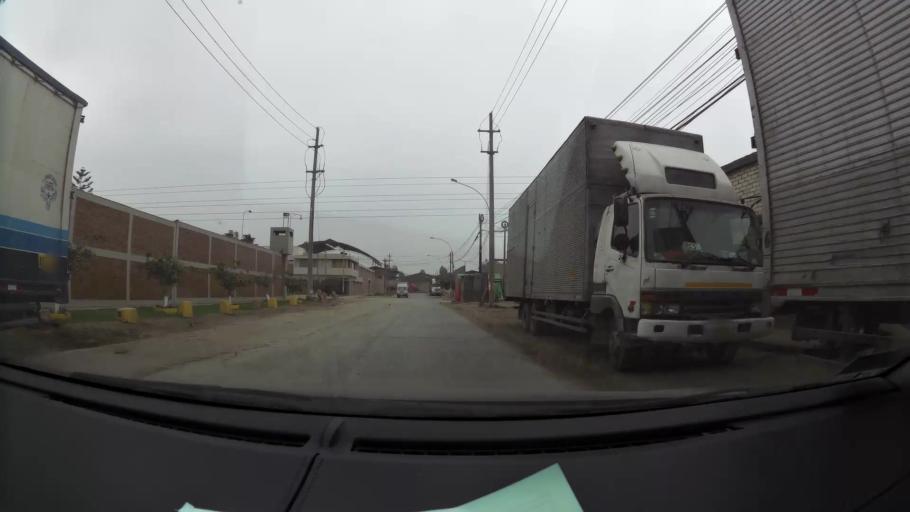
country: PE
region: Lima
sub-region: Lima
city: Carabayllo
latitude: -11.8667
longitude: -77.0710
